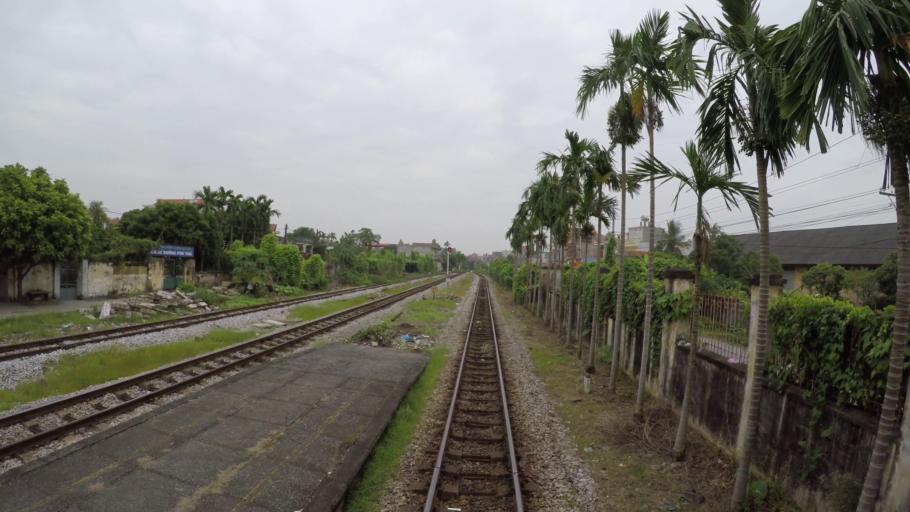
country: VN
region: Hai Duong
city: Phu Thai
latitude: 20.9705
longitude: 106.4961
